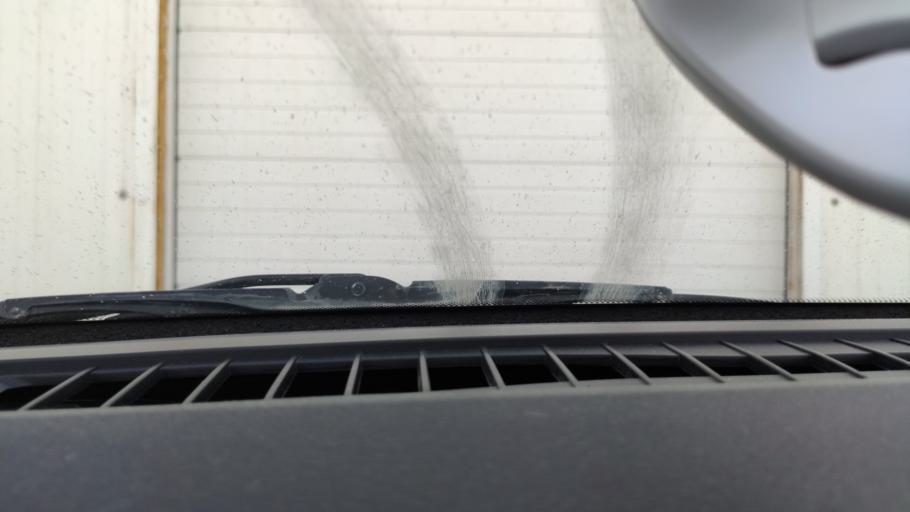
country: RU
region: Perm
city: Perm
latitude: 58.0389
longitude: 56.2026
